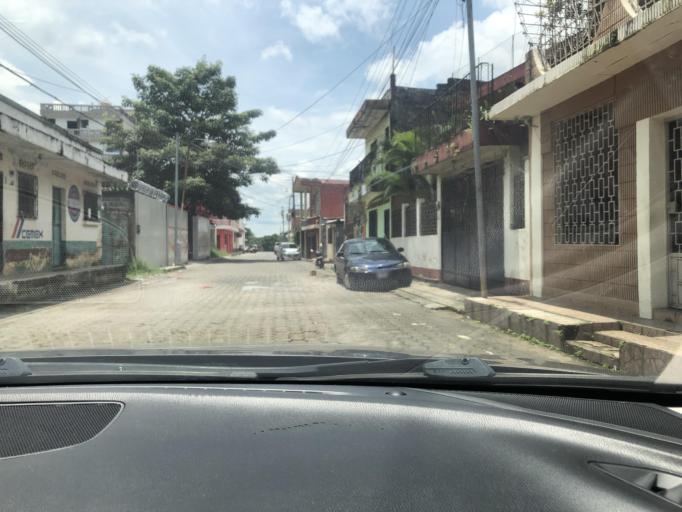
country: GT
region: Quetzaltenango
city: Coatepeque
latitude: 14.7090
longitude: -91.8653
